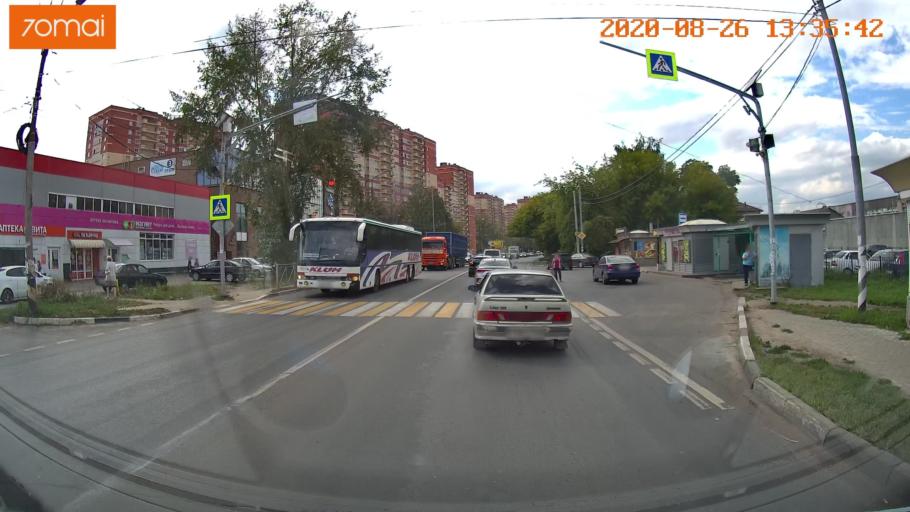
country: RU
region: Rjazan
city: Ryazan'
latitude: 54.6186
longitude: 39.6701
